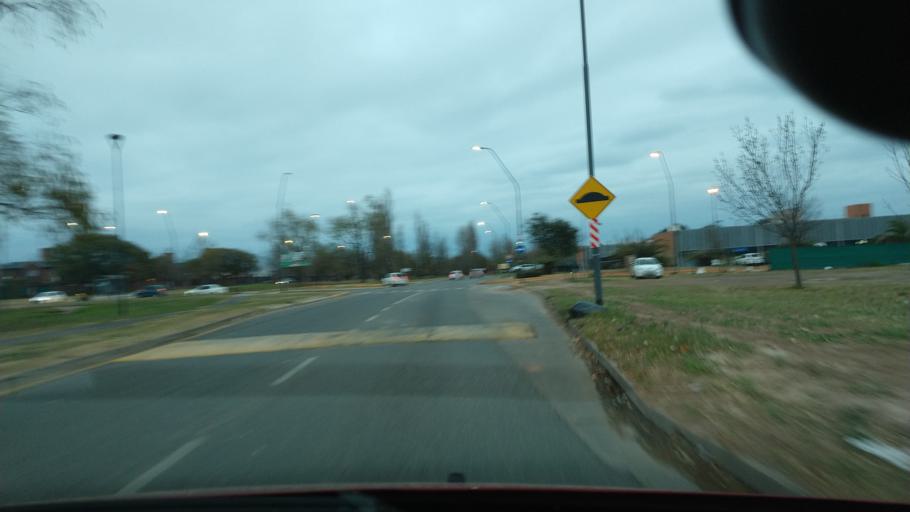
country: AR
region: Cordoba
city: La Calera
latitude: -31.3739
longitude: -64.2774
